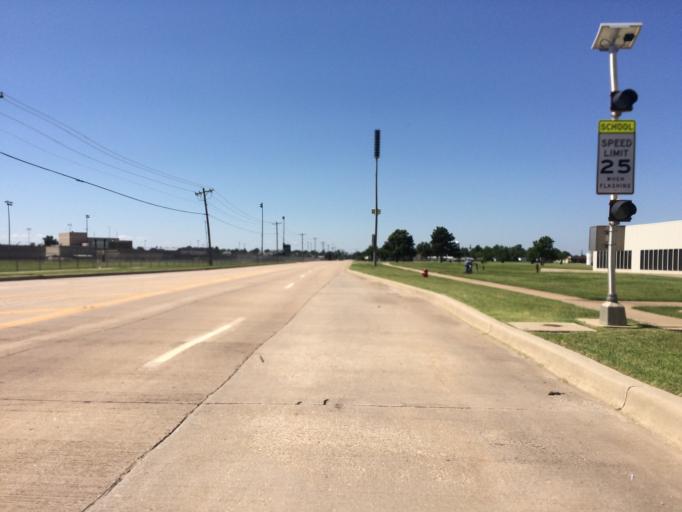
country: US
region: Oklahoma
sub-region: Cleveland County
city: Norman
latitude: 35.2466
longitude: -97.4501
